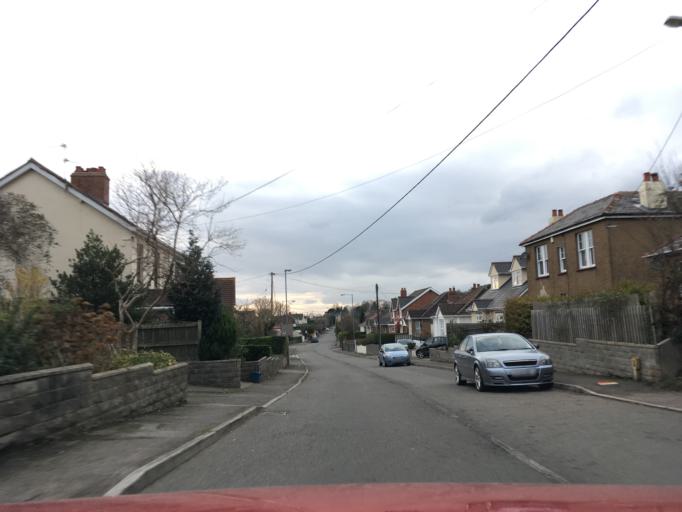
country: GB
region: Wales
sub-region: Monmouthshire
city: Caldicot
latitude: 51.5921
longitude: -2.7160
